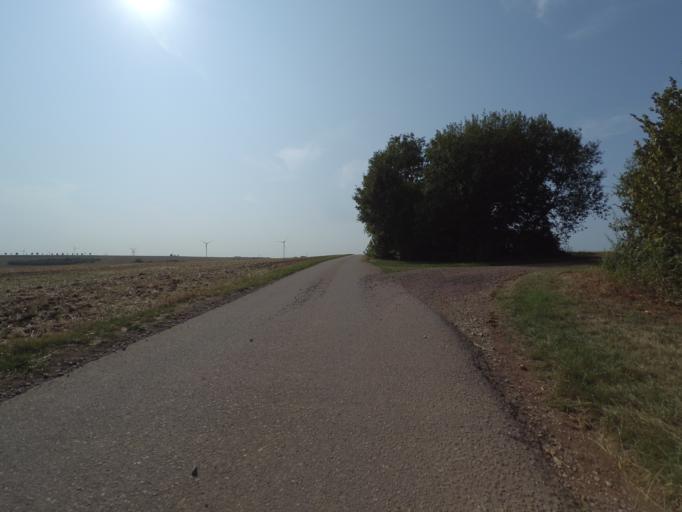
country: DE
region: Saarland
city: Perl
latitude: 49.4820
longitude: 6.4419
